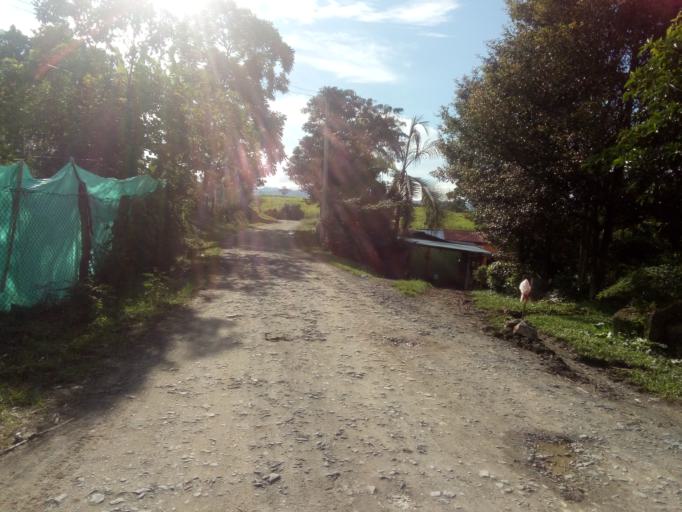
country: CO
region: Boyaca
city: Santana
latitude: 6.0438
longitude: -73.5011
